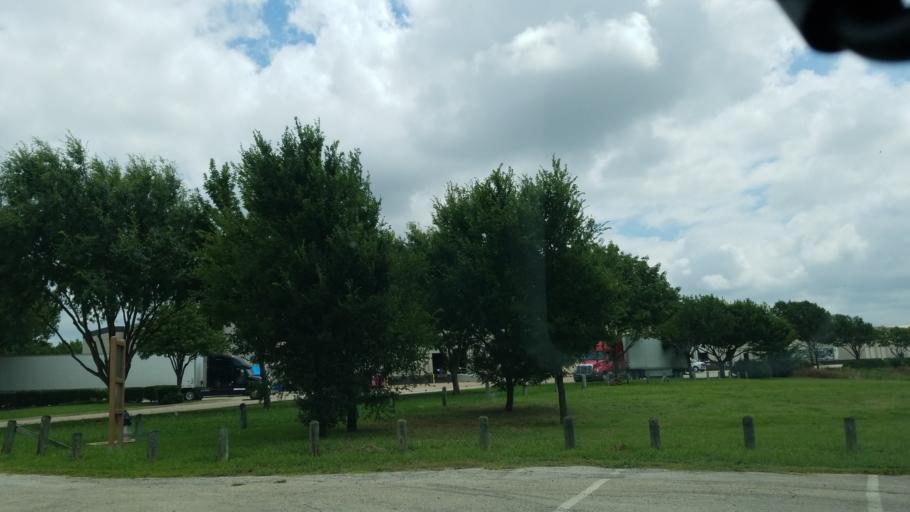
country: US
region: Texas
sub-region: Dallas County
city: Farmers Branch
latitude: 32.9488
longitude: -96.9367
